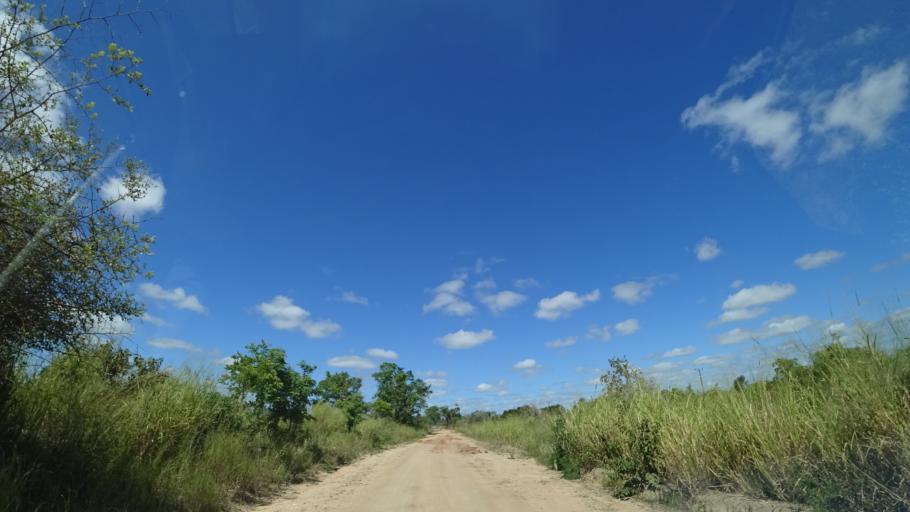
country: MZ
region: Sofala
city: Dondo
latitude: -19.2804
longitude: 34.6837
